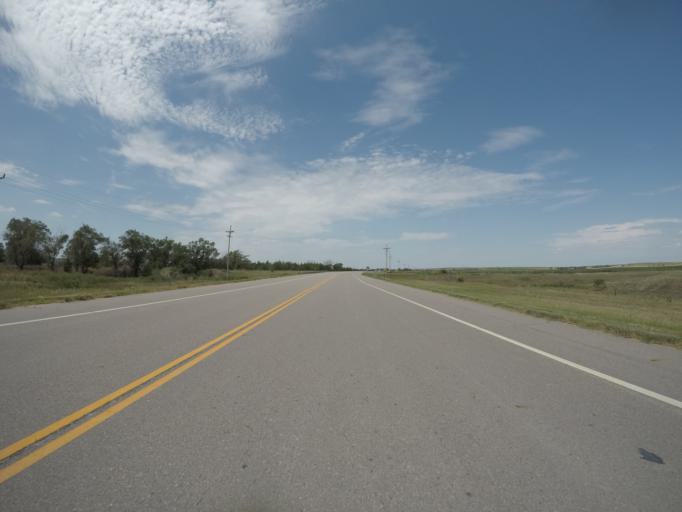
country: US
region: Kansas
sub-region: Rooks County
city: Stockton
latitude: 39.4551
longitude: -99.1040
